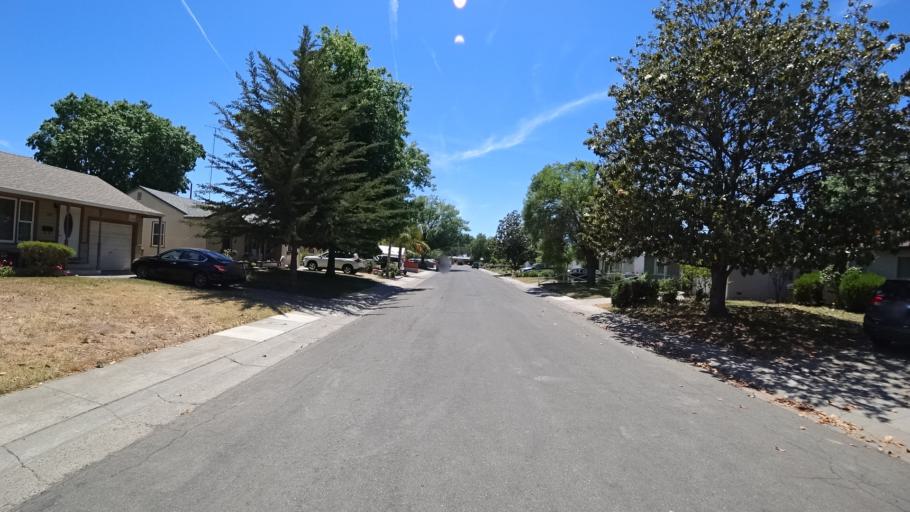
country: US
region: California
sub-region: Sacramento County
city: Parkway
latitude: 38.5231
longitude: -121.4966
